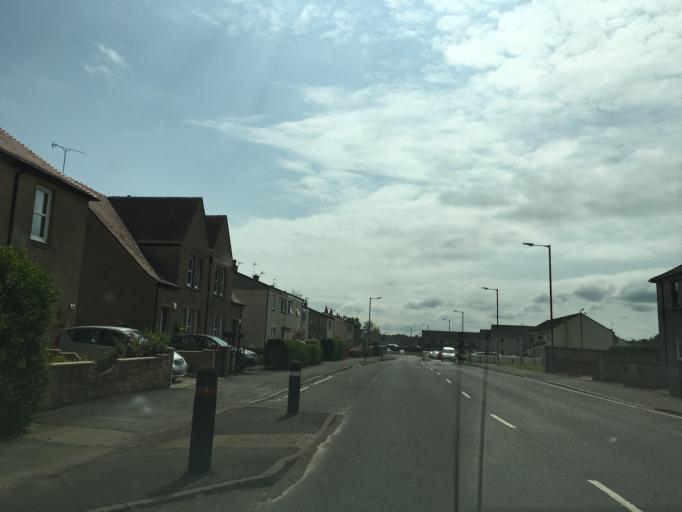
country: GB
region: Scotland
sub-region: Stirling
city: Stirling
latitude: 56.1103
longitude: -3.9292
